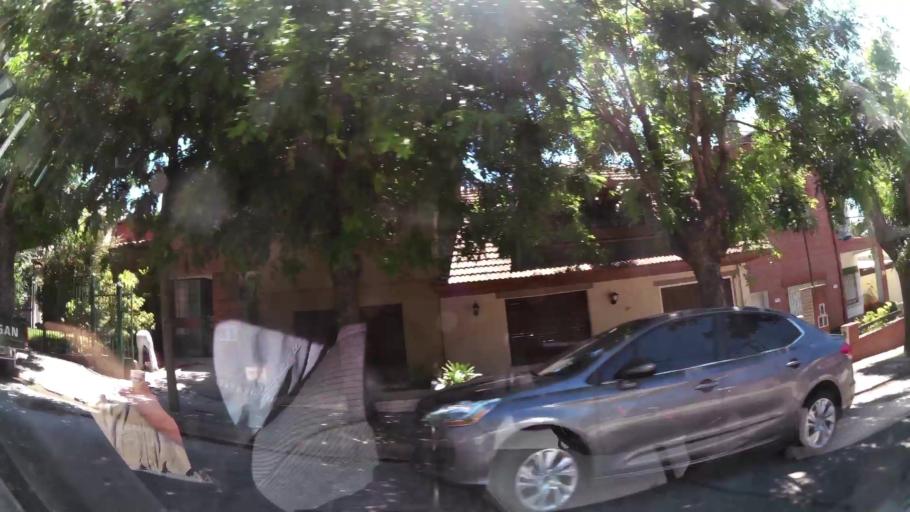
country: AR
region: Buenos Aires
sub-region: Partido de Tigre
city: Tigre
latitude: -34.4415
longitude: -58.5496
